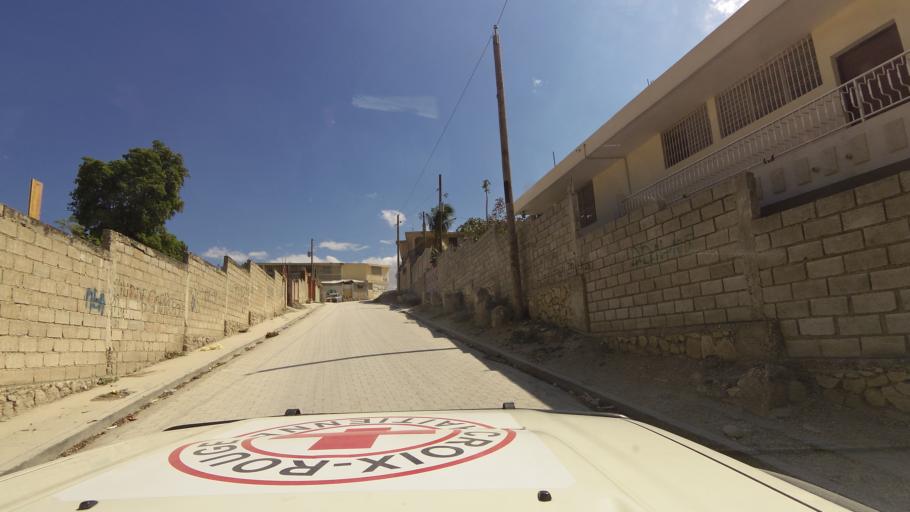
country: HT
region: Ouest
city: Delmas 73
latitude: 18.5533
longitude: -72.2961
